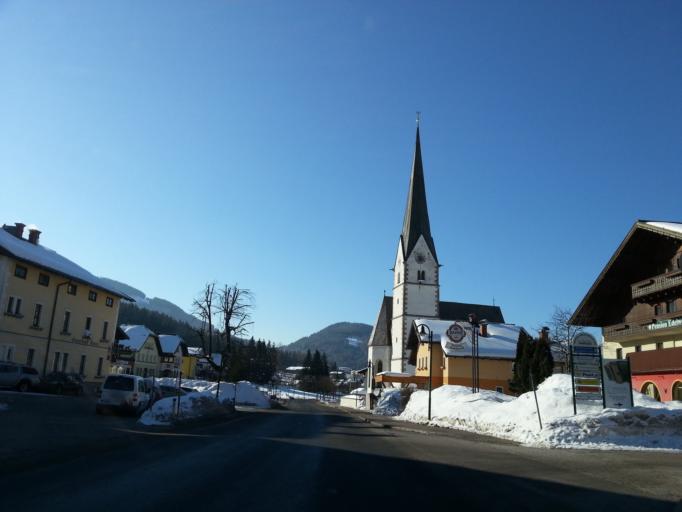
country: AT
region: Salzburg
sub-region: Politischer Bezirk Sankt Johann im Pongau
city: Eben im Pongau
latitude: 47.4656
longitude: 13.3810
